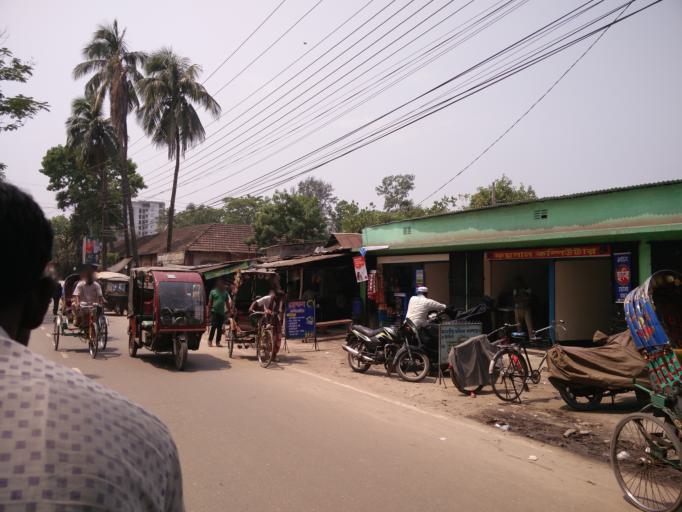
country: BD
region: Dhaka
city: Mymensingh
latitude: 24.7635
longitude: 90.4055
